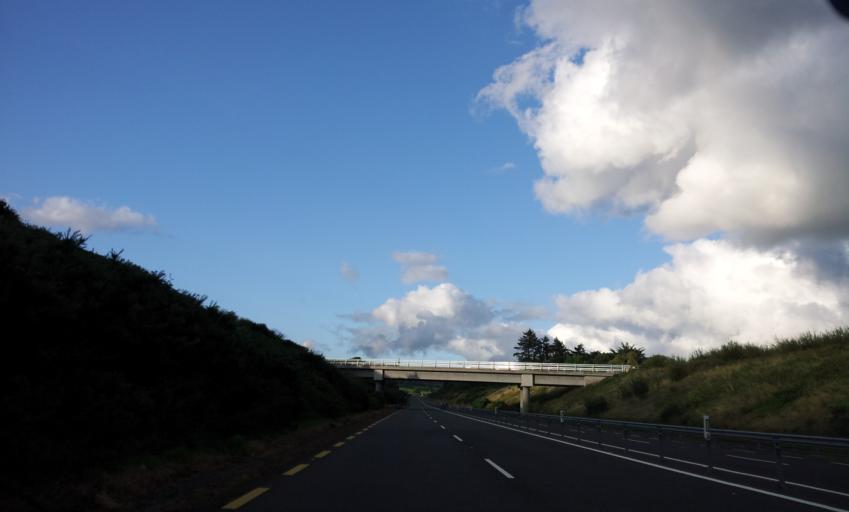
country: IE
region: Munster
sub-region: Ciarrai
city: Castleisland
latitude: 52.2492
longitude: -9.4800
